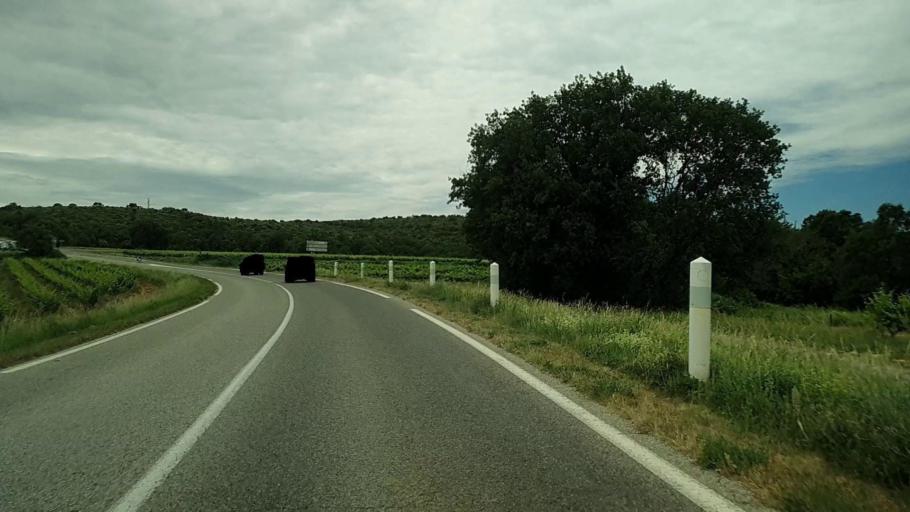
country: FR
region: Languedoc-Roussillon
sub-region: Departement du Gard
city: Sabran
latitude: 44.1378
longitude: 4.4752
